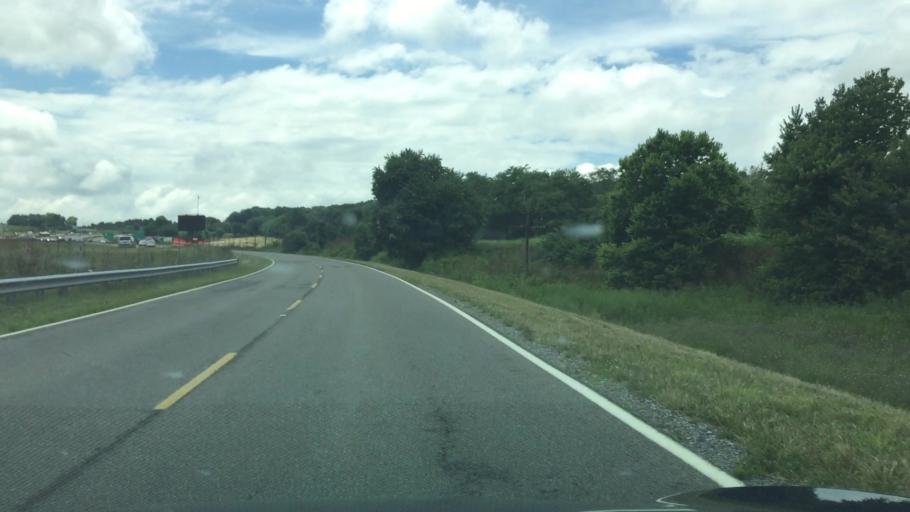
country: US
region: Virginia
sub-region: Wythe County
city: Wytheville
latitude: 36.9470
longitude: -81.0349
